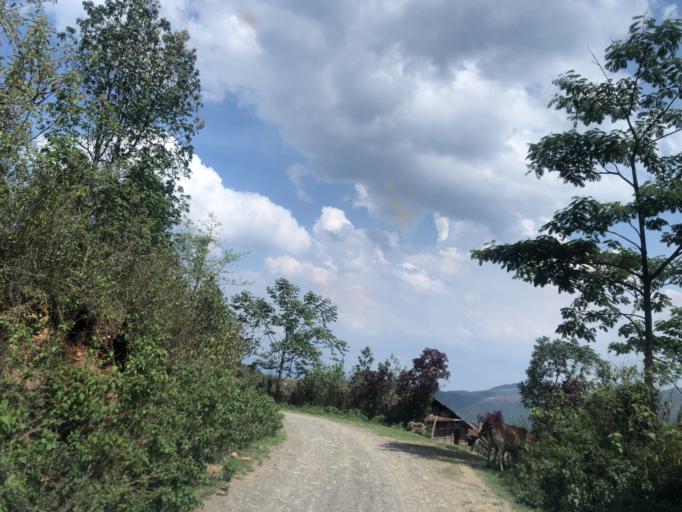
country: LA
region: Phongsali
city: Phongsali
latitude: 21.4083
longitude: 102.2345
